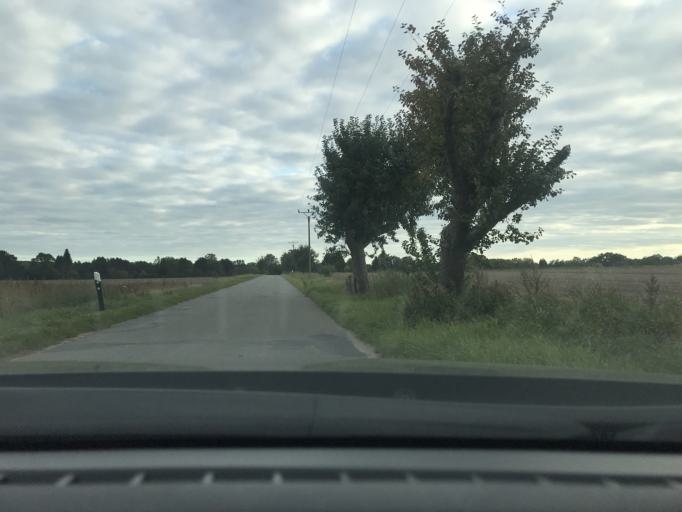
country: DE
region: Lower Saxony
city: Suderburg
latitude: 52.9029
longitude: 10.4540
